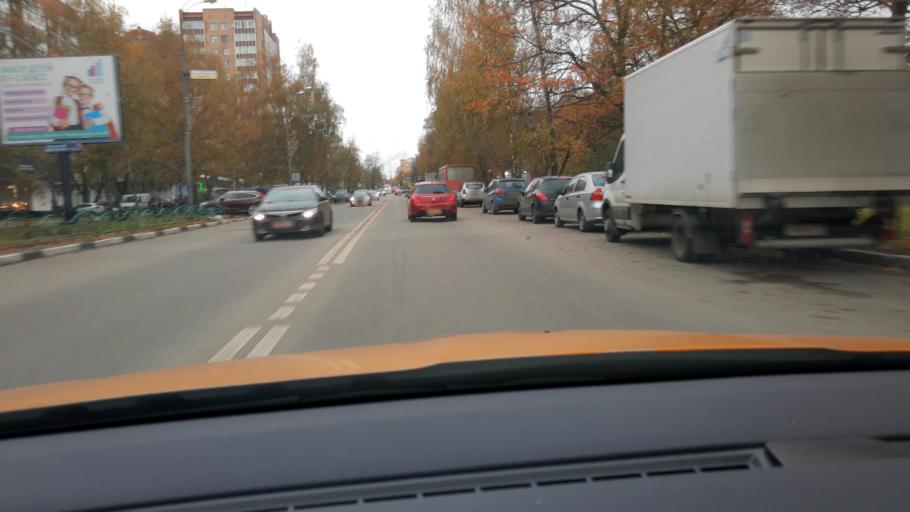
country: RU
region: Moskovskaya
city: Odintsovo
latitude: 55.6748
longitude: 37.2716
